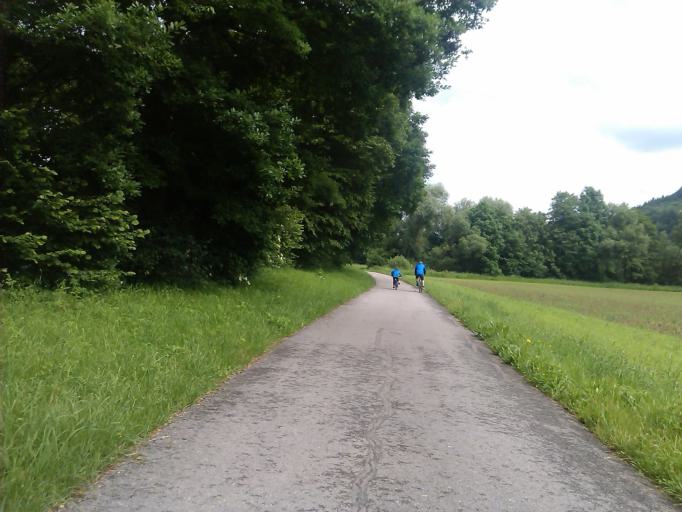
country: DE
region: Baden-Wuerttemberg
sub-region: Regierungsbezirk Stuttgart
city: Gaildorf
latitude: 48.9746
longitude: 9.8068
